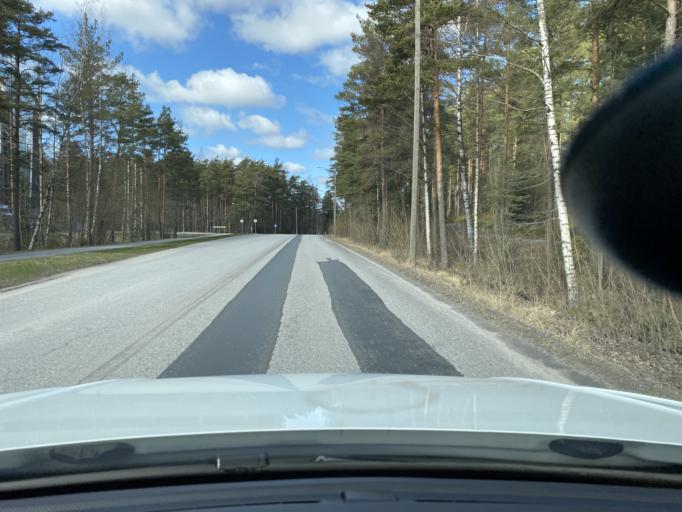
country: FI
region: Varsinais-Suomi
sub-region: Turku
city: Turku
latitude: 60.4779
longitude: 22.3167
